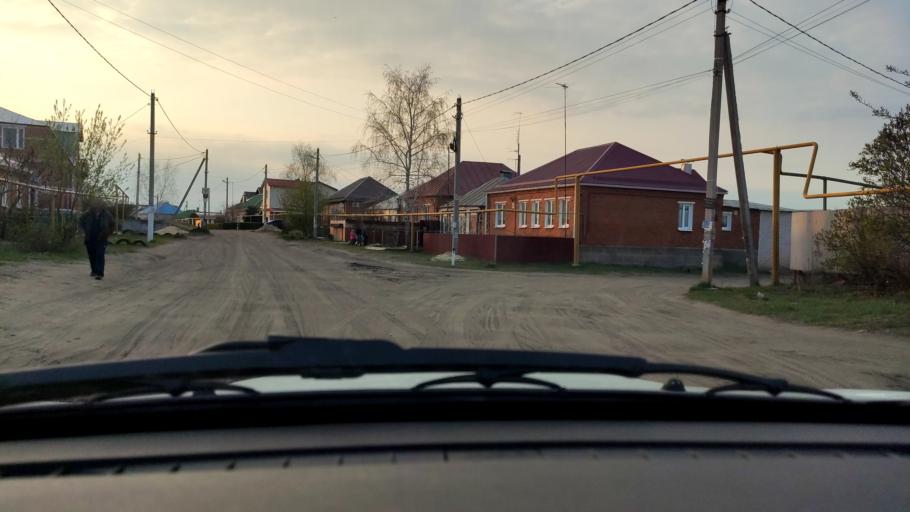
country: RU
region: Voronezj
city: Somovo
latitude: 51.7504
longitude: 39.3342
